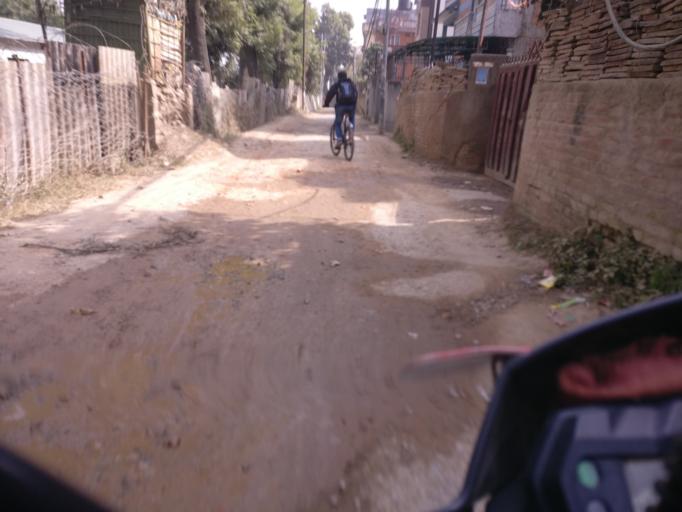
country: NP
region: Central Region
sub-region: Bagmati Zone
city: Patan
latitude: 27.6620
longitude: 85.3208
